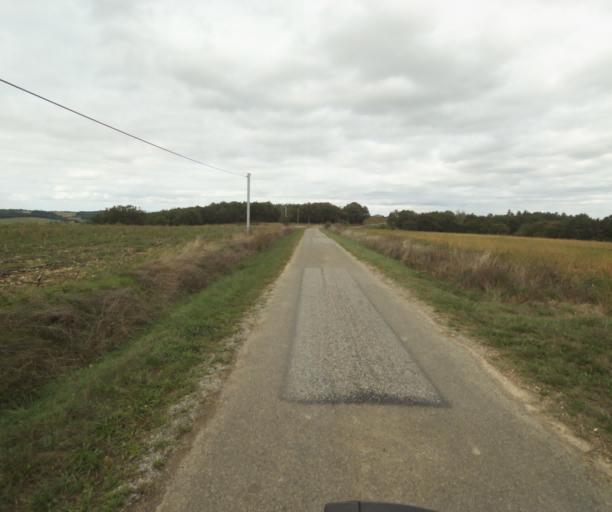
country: FR
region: Midi-Pyrenees
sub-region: Departement du Tarn-et-Garonne
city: Beaumont-de-Lomagne
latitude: 43.8416
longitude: 1.0950
